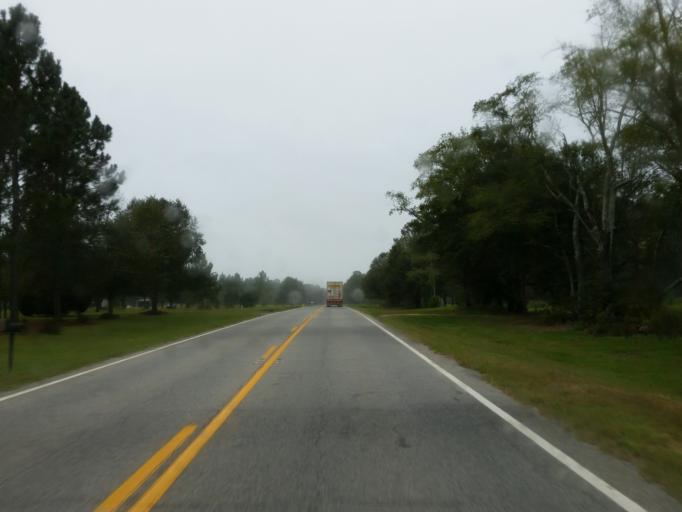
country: US
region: Georgia
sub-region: Berrien County
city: Ray City
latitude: 31.1010
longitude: -83.2732
